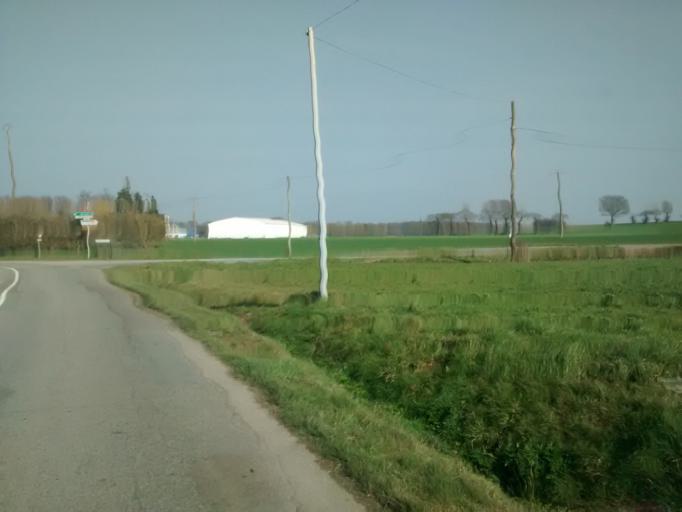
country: FR
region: Brittany
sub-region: Departement d'Ille-et-Vilaine
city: Saint-Thurial
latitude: 48.0537
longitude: -1.9080
